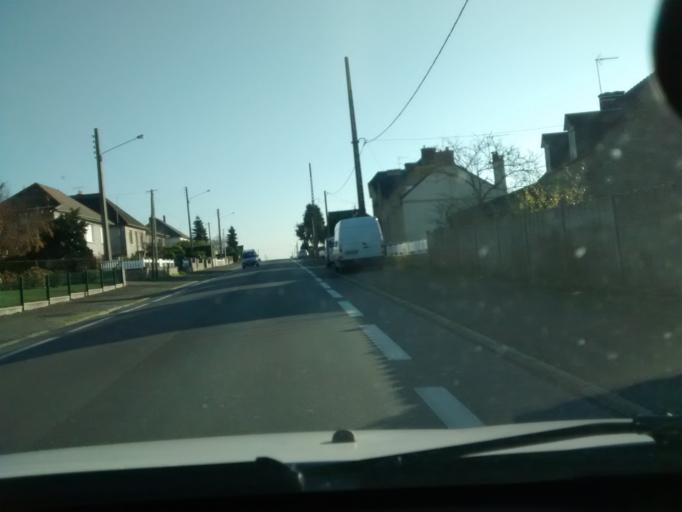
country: FR
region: Lower Normandy
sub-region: Departement de la Manche
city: Pontorson
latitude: 48.5463
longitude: -1.5015
